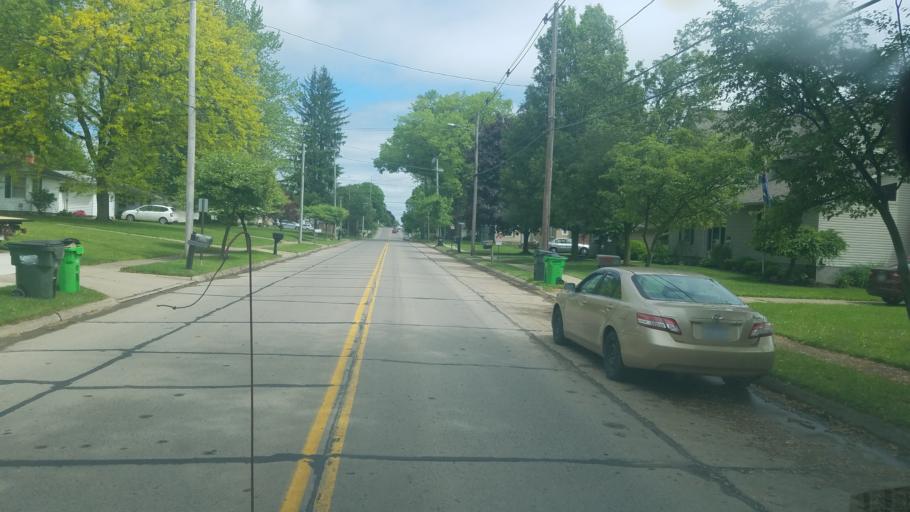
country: US
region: Ohio
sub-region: Wayne County
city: Orrville
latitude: 40.8415
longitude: -81.7845
